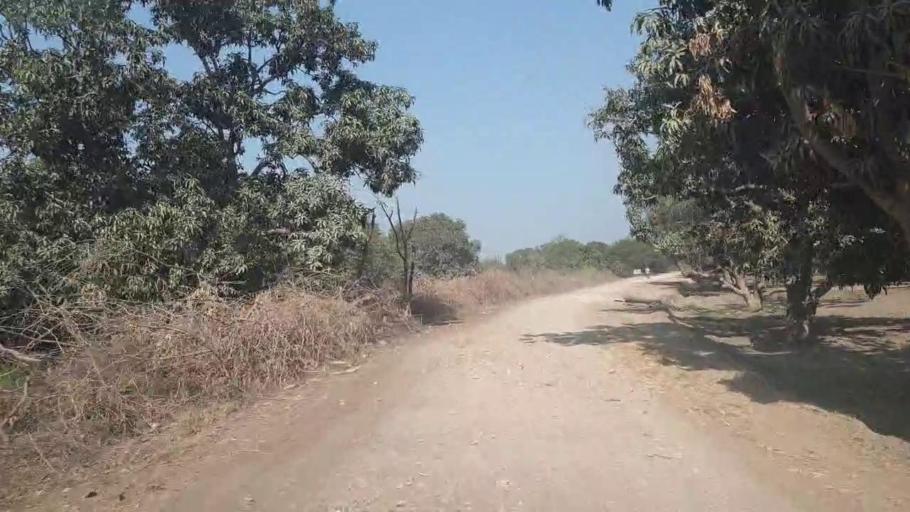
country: PK
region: Sindh
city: Tando Allahyar
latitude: 25.4513
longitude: 68.8320
